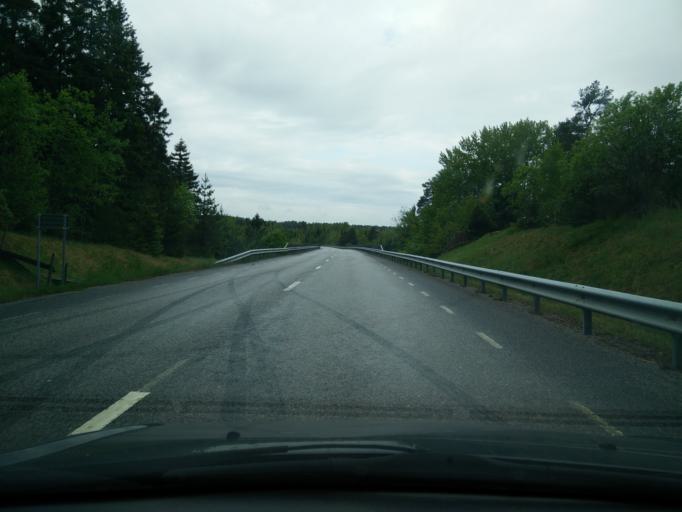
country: SE
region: Stockholm
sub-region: Norrtalje Kommun
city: Bjorko
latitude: 59.8183
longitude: 18.9199
